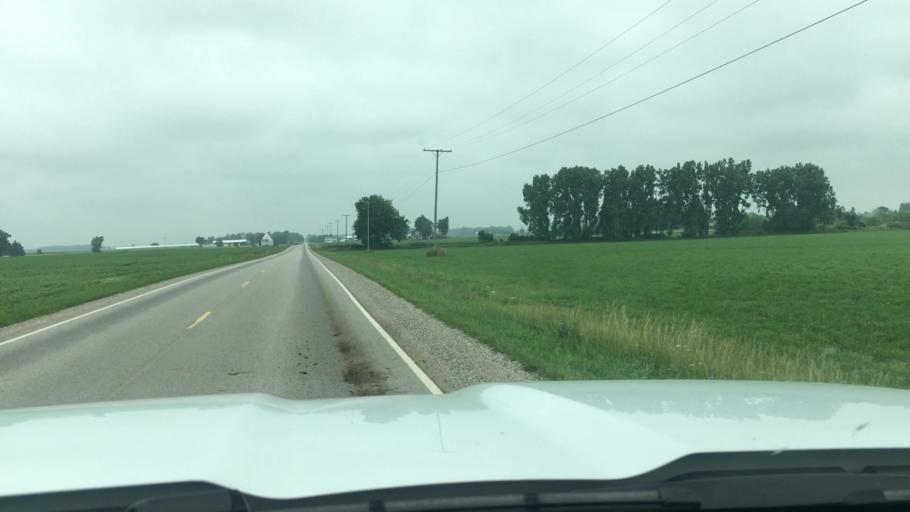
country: US
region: Michigan
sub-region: Sanilac County
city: Brown City
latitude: 43.2791
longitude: -82.9827
